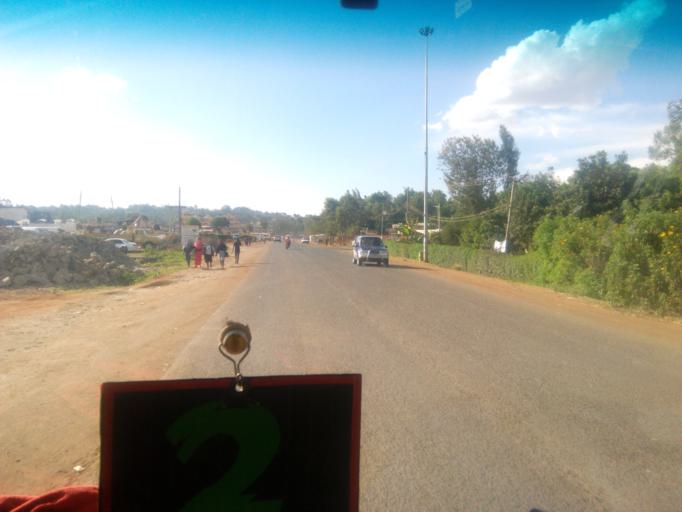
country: KE
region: Kiambu
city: Kikuyu
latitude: -1.2793
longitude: 36.6891
